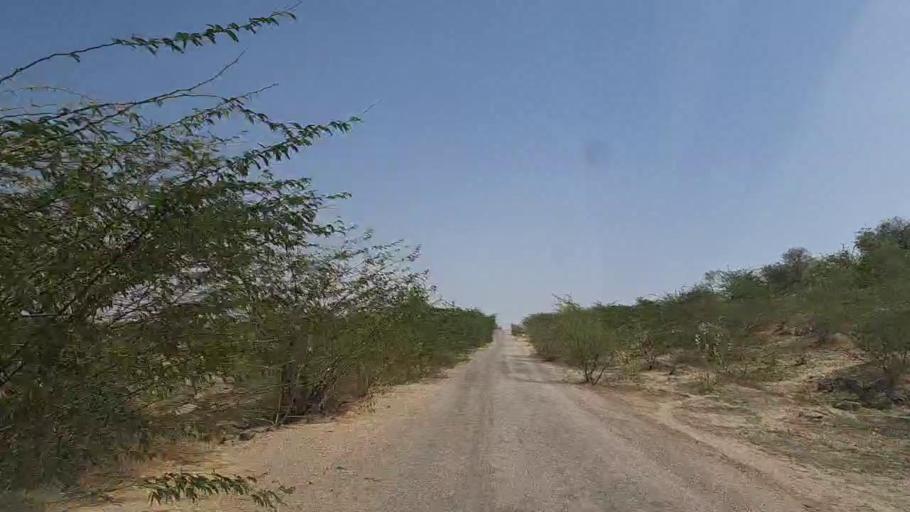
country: PK
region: Sindh
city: Diplo
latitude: 24.4856
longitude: 69.4640
